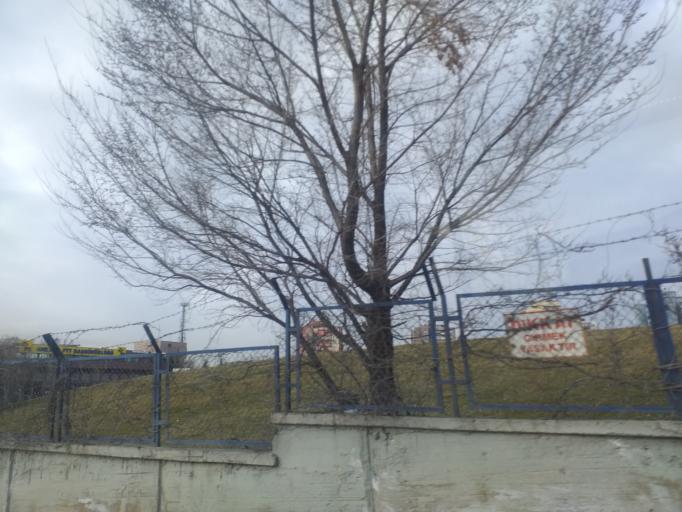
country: TR
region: Ankara
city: Ankara
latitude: 39.9584
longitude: 32.8233
